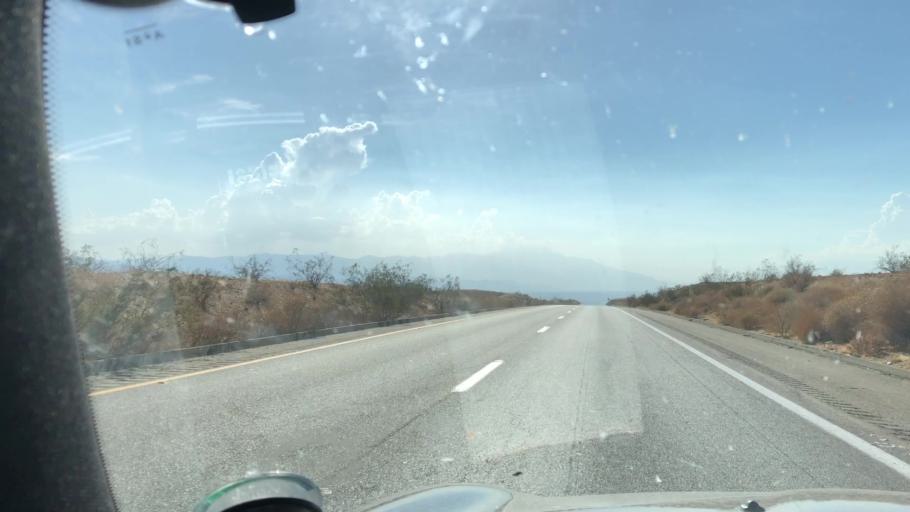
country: US
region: California
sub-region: Riverside County
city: Thermal
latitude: 33.6880
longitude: -116.0322
